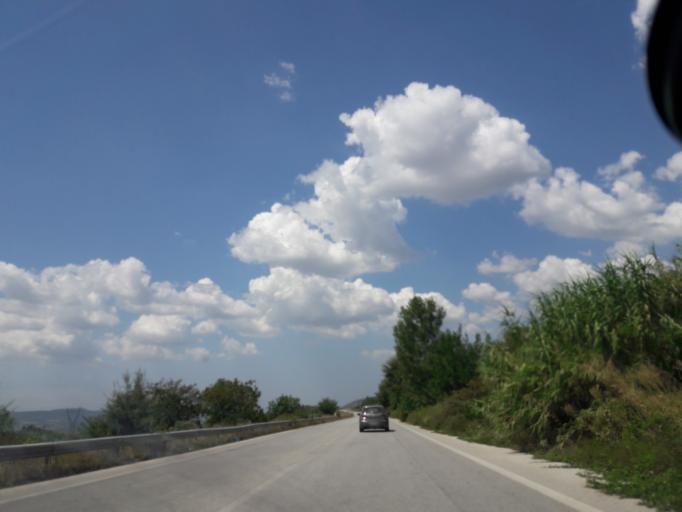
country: GR
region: Central Macedonia
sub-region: Nomos Chalkidikis
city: Galatista
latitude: 40.4618
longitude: 23.2792
